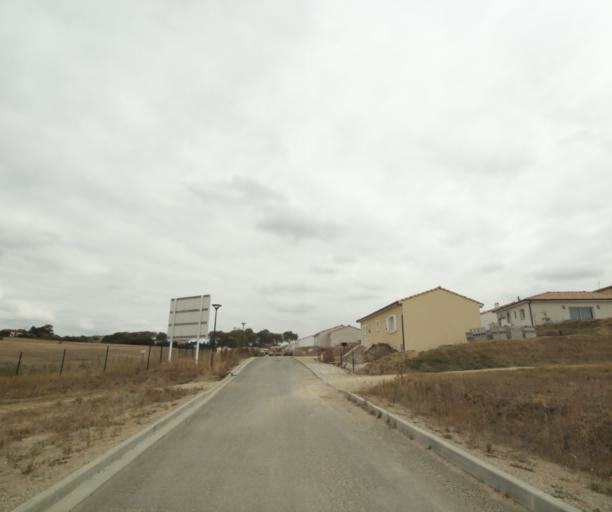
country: FR
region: Midi-Pyrenees
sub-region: Departement de la Haute-Garonne
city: Villefranche-de-Lauragais
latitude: 43.4053
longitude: 1.7204
